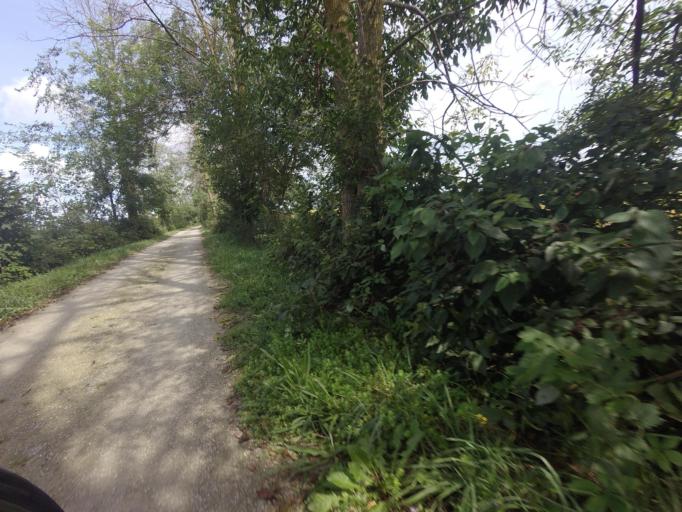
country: CA
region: Ontario
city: Waterloo
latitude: 43.6086
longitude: -80.6165
